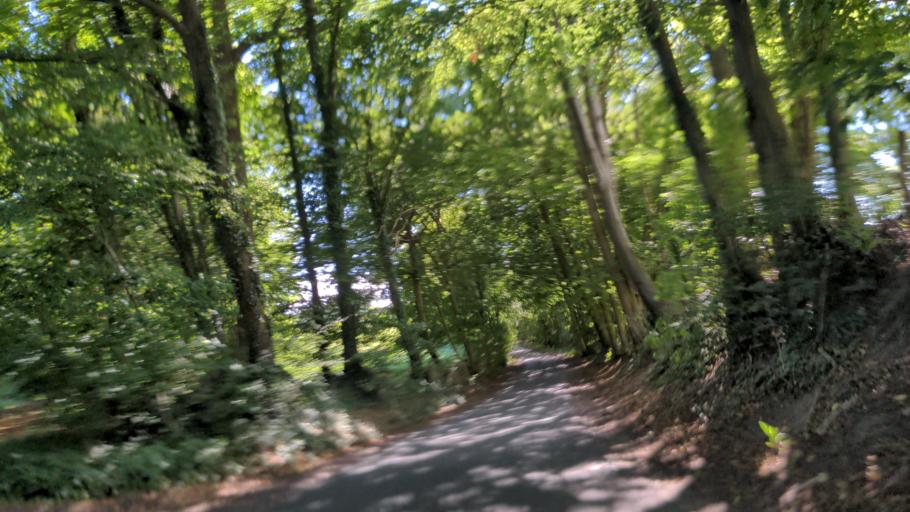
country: DE
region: Schleswig-Holstein
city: Kasseedorf
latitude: 54.1397
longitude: 10.7242
